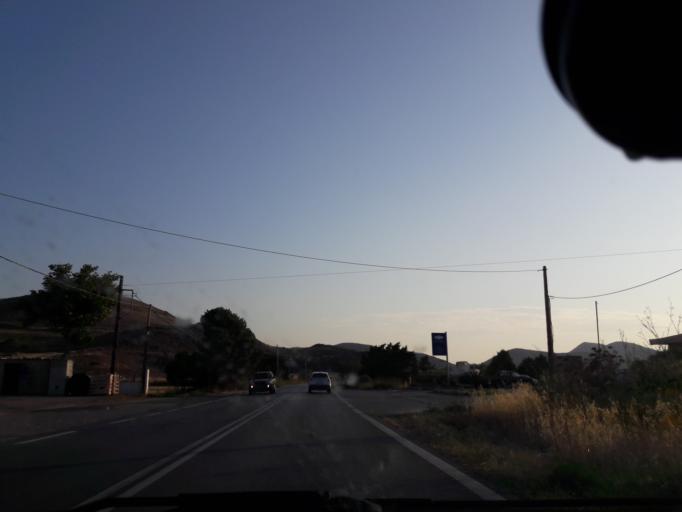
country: GR
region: North Aegean
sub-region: Nomos Lesvou
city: Myrina
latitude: 39.8988
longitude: 25.1002
